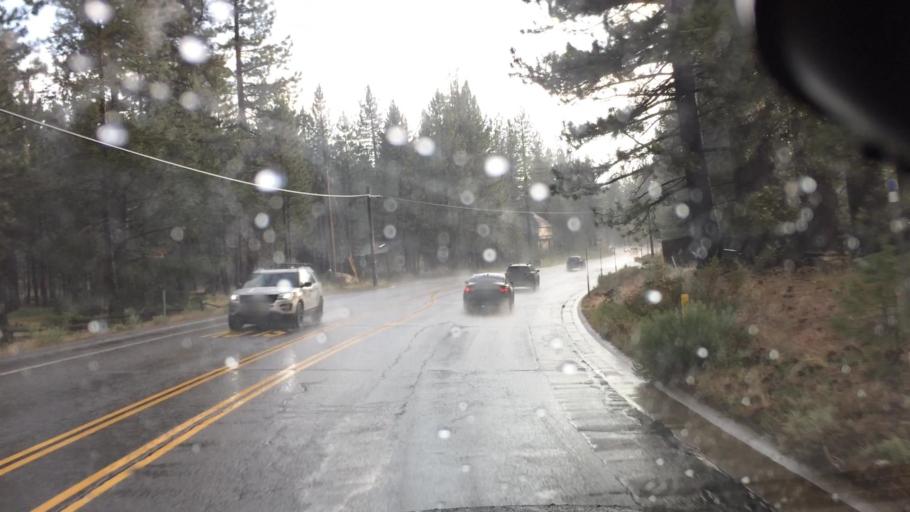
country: US
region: California
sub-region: El Dorado County
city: South Lake Tahoe
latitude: 38.9062
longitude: -119.9653
